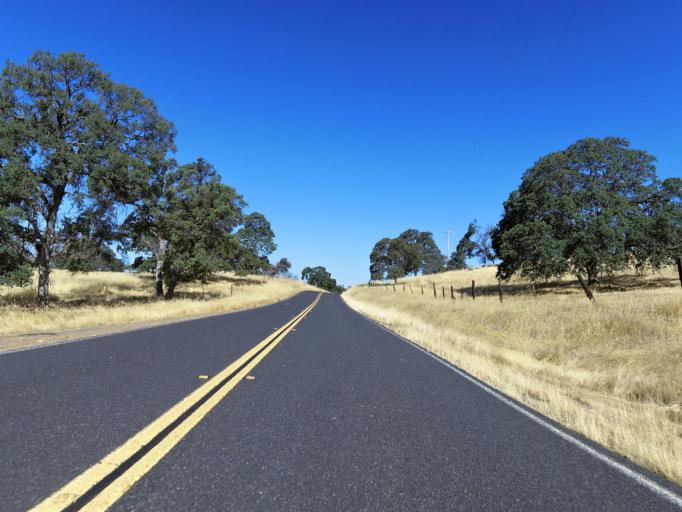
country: US
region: California
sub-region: Mariposa County
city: Mariposa
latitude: 37.4941
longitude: -120.1552
